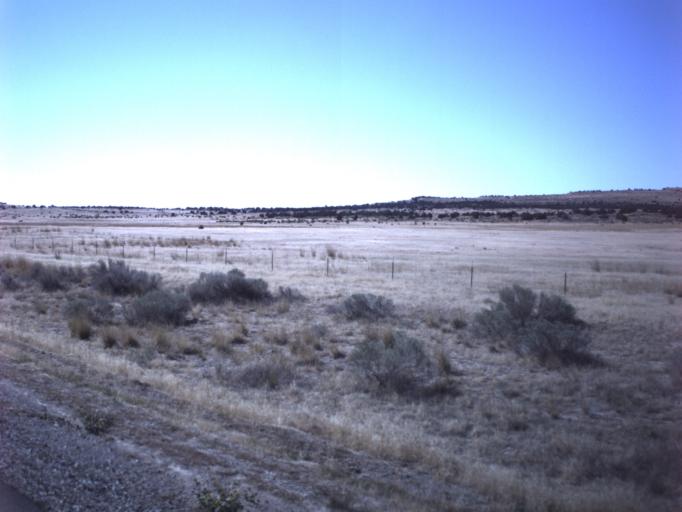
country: US
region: Utah
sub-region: Tooele County
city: Grantsville
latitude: 40.2595
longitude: -112.7406
